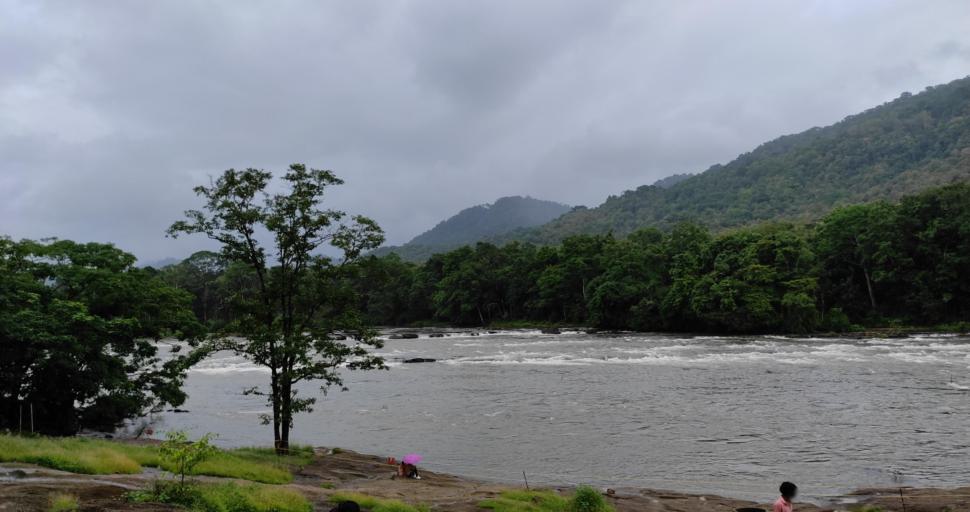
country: IN
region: Kerala
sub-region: Ernakulam
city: Angamali
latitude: 10.2859
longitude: 76.5707
